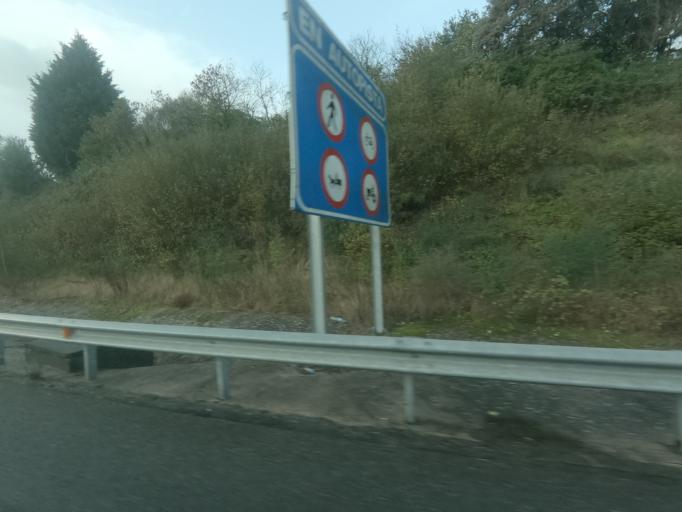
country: ES
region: Galicia
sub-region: Provincia de Pontevedra
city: Tui
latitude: 42.0674
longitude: -8.6413
